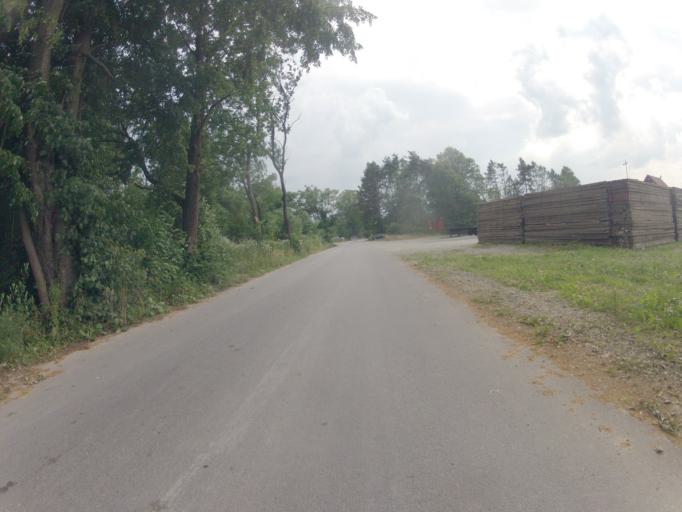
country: PL
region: Lesser Poland Voivodeship
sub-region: Powiat nowosadecki
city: Stary Sacz
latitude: 49.5560
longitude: 20.6596
